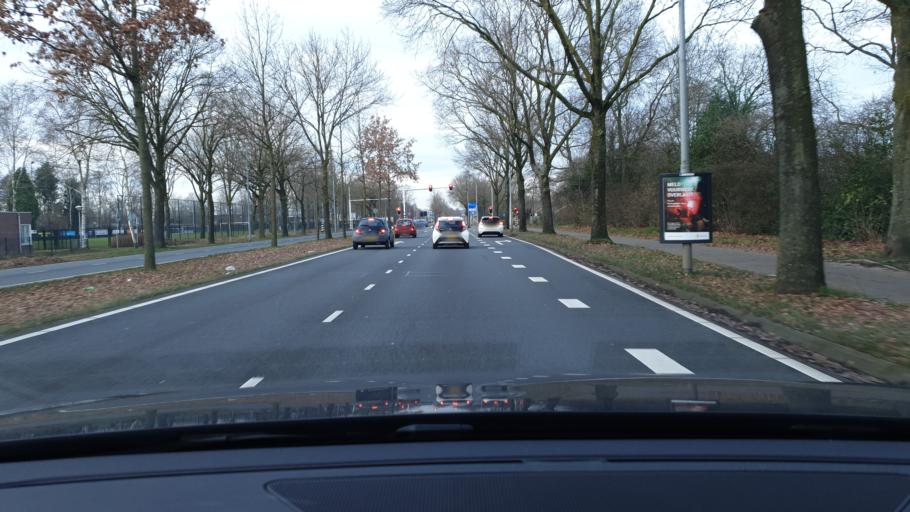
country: NL
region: North Brabant
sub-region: Gemeente Eindhoven
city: Meerhoven
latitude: 51.4821
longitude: 5.4345
